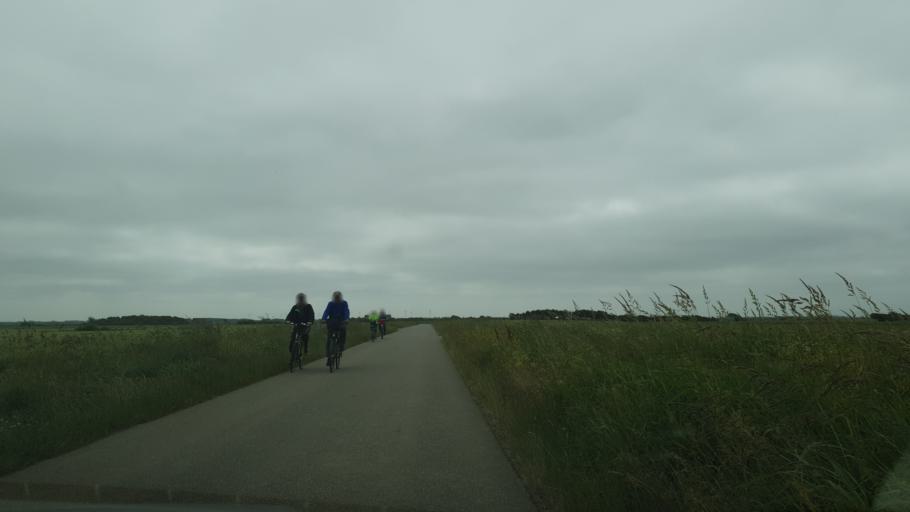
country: DK
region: Central Jutland
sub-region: Ringkobing-Skjern Kommune
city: Skjern
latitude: 55.9274
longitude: 8.4027
